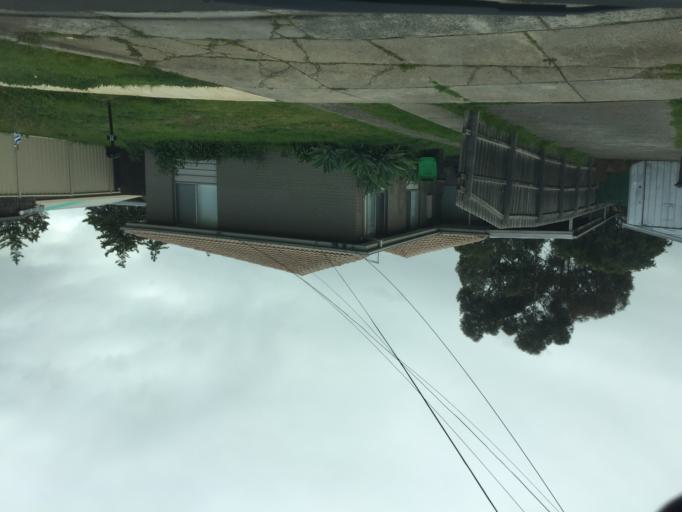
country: AU
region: Victoria
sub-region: Brimbank
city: Sunshine West
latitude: -37.8026
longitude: 144.8299
